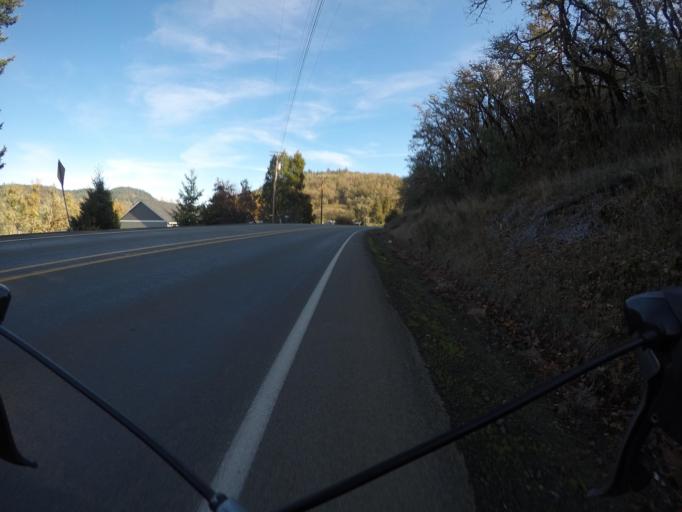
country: US
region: Oregon
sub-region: Douglas County
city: Winston
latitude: 43.1873
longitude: -123.4569
